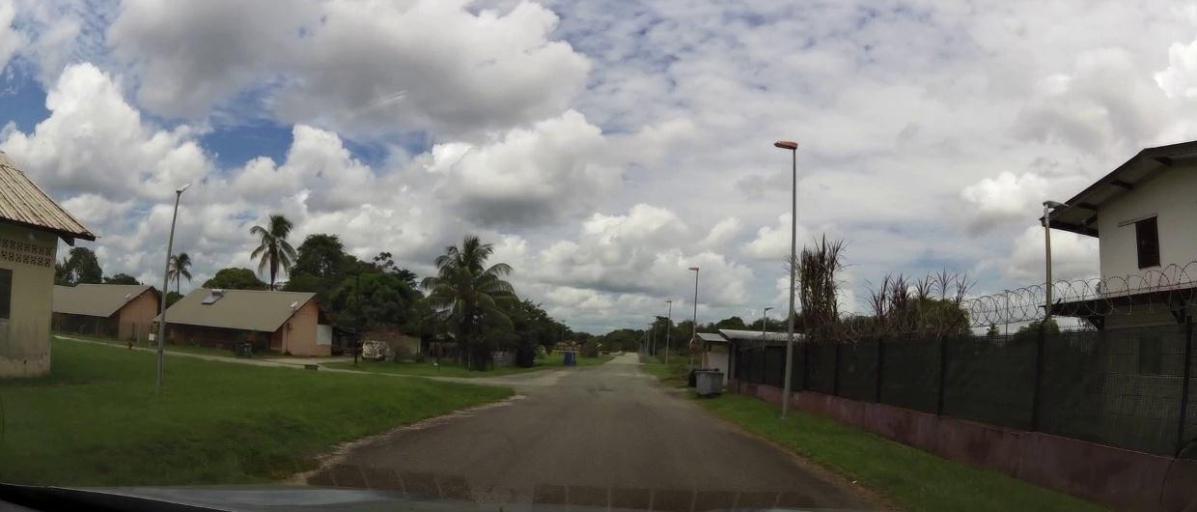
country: GF
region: Guyane
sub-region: Guyane
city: Sinnamary
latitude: 5.3736
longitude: -52.9522
